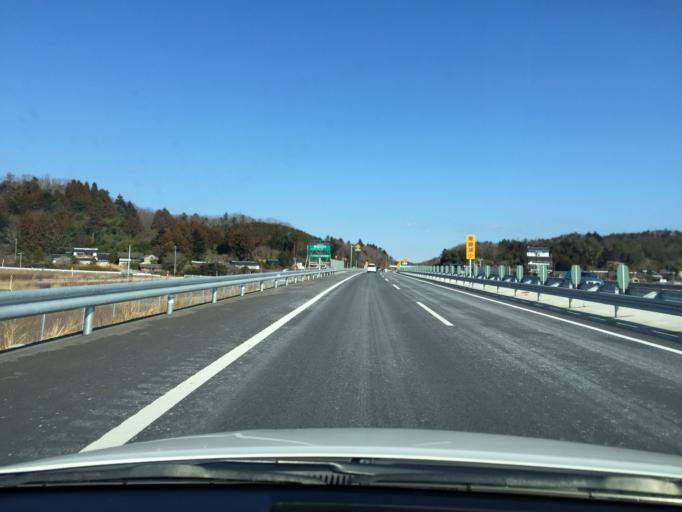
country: JP
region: Fukushima
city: Namie
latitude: 37.4109
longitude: 140.9621
